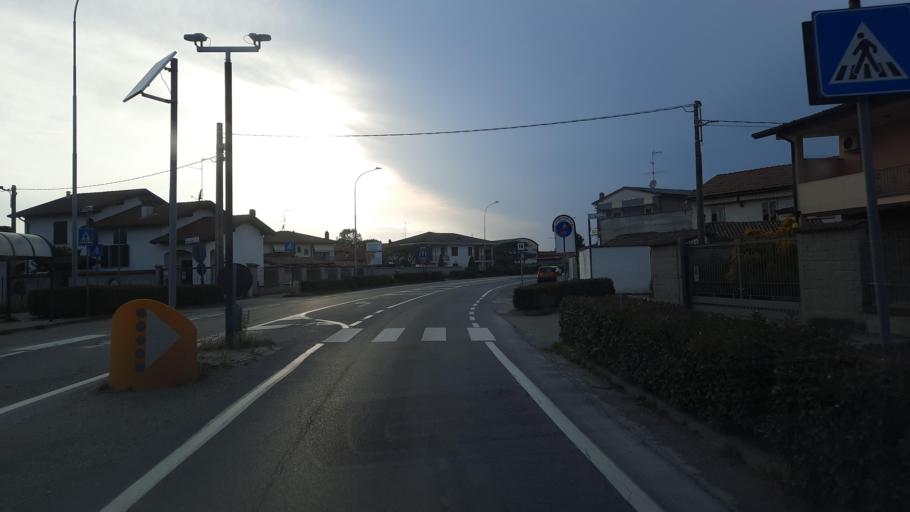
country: IT
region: Lombardy
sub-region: Provincia di Pavia
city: Garlasco
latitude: 45.1927
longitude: 8.9155
